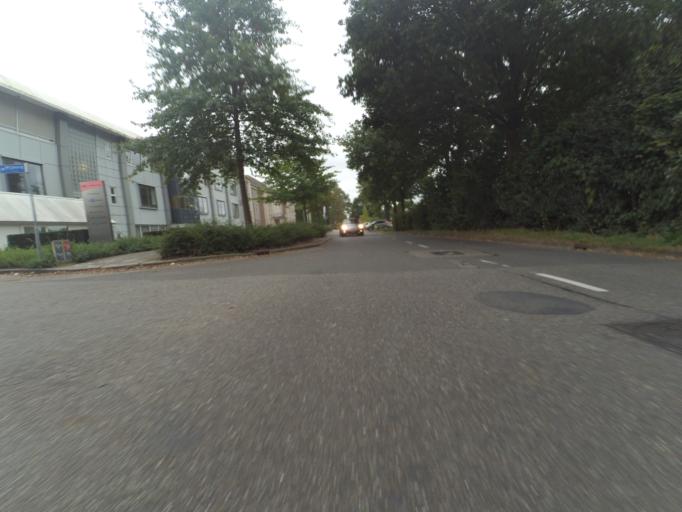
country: NL
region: Gelderland
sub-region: Gemeente Ede
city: Ederveen
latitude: 52.0744
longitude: 5.5309
